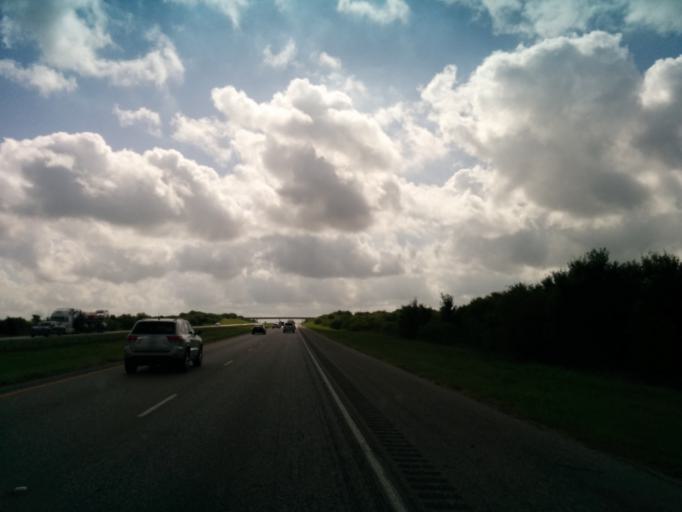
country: US
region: Texas
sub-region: Gonzales County
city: Waelder
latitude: 29.6659
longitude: -97.3417
